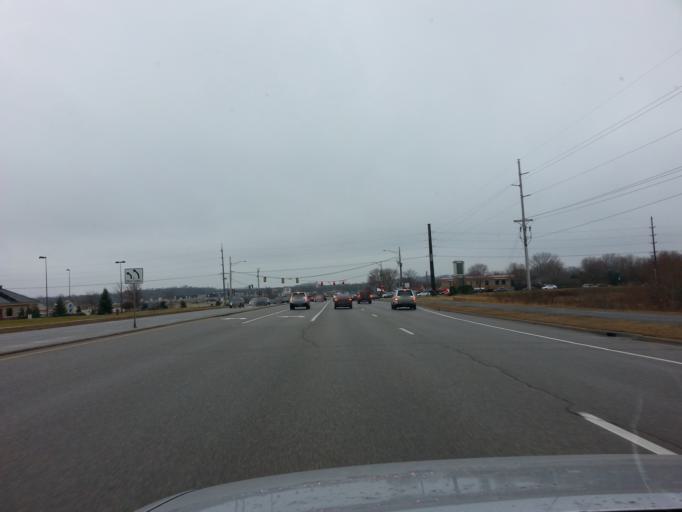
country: US
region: Minnesota
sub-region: Scott County
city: Savage
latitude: 44.7479
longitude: -93.3798
